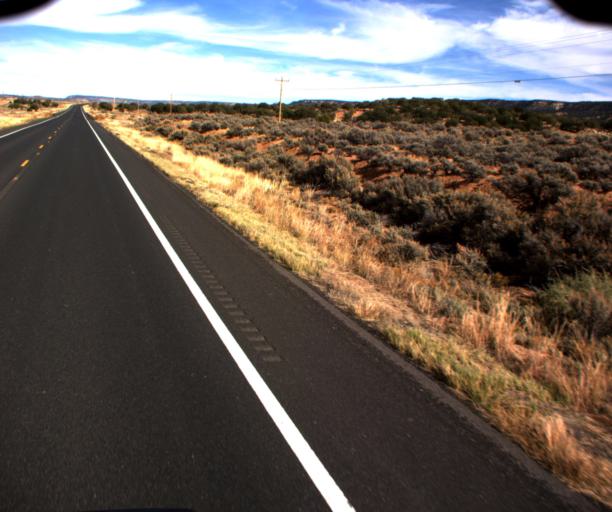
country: US
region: Arizona
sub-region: Navajo County
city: Kayenta
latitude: 36.5138
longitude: -110.5981
